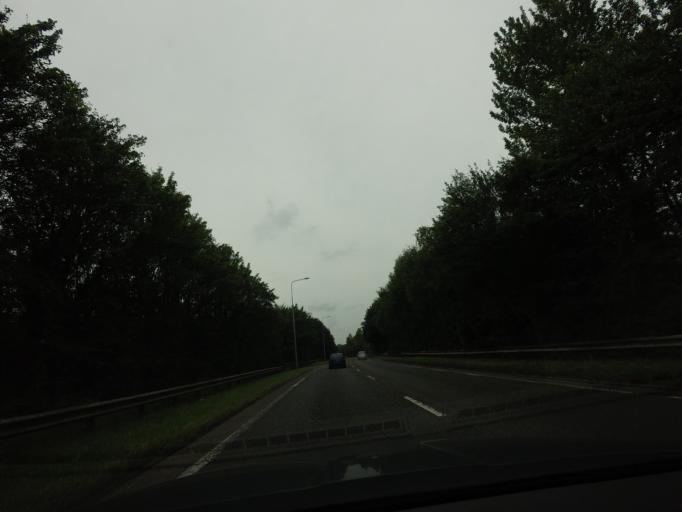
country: GB
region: England
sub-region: Telford and Wrekin
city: Madeley
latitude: 52.6458
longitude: -2.4478
